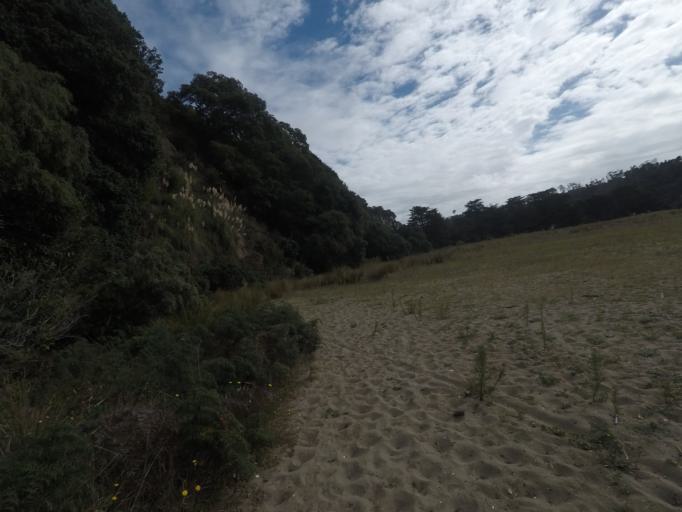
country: NZ
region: Auckland
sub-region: Auckland
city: Rothesay Bay
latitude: -36.6470
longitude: 174.7255
